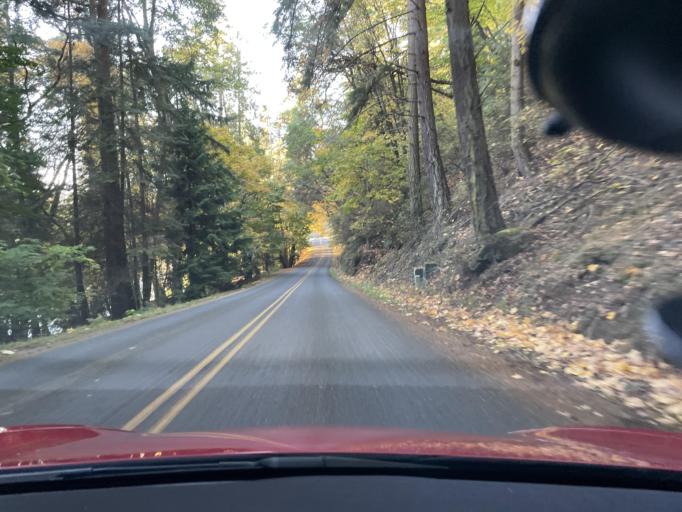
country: US
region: Washington
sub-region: San Juan County
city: Friday Harbor
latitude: 48.5394
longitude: -123.1584
